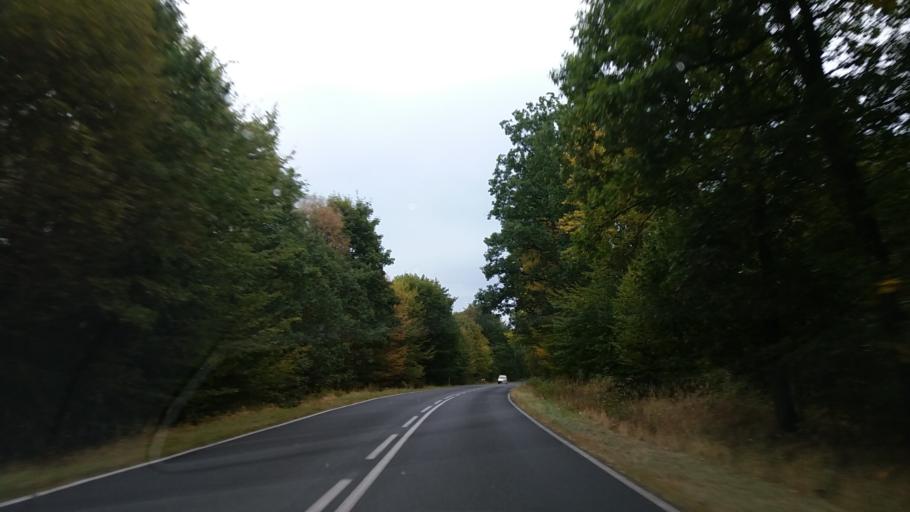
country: PL
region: West Pomeranian Voivodeship
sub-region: Powiat mysliborski
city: Barlinek
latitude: 52.9003
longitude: 15.1928
